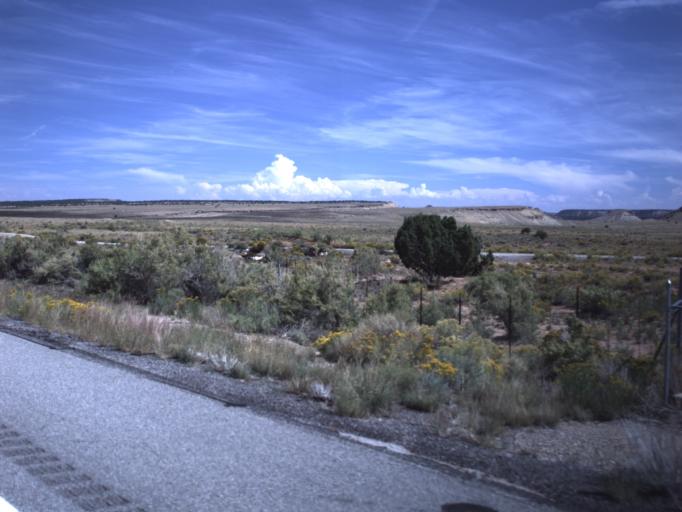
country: US
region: Utah
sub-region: Emery County
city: Castle Dale
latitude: 38.8709
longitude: -110.6898
